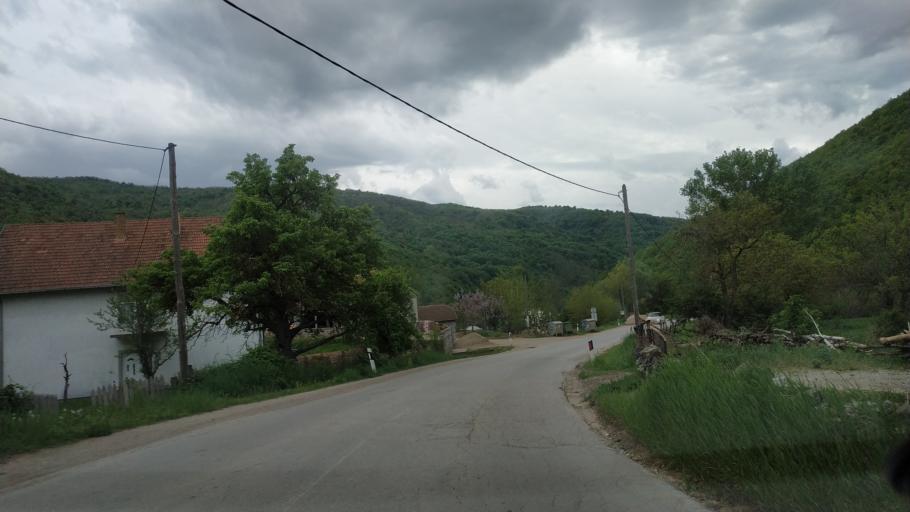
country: RS
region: Central Serbia
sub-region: Nisavski Okrug
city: Aleksinac
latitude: 43.6337
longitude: 21.7185
